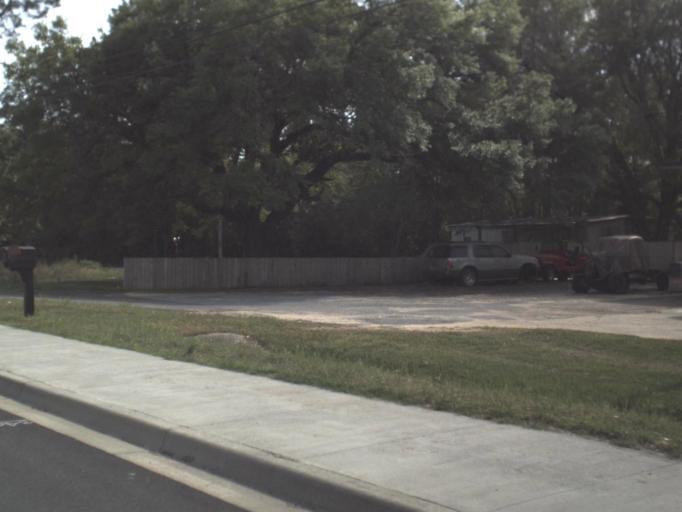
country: US
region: Florida
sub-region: Santa Rosa County
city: Holley
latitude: 30.4578
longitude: -86.9097
